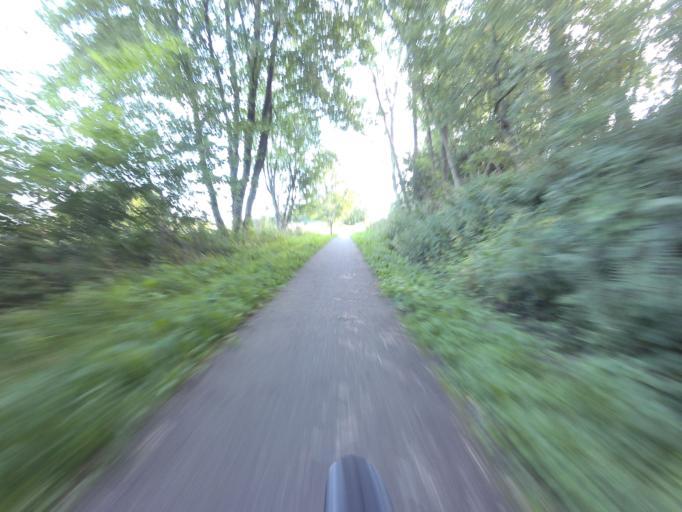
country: DK
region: Central Jutland
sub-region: Horsens Kommune
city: Horsens
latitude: 55.9387
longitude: 9.7772
